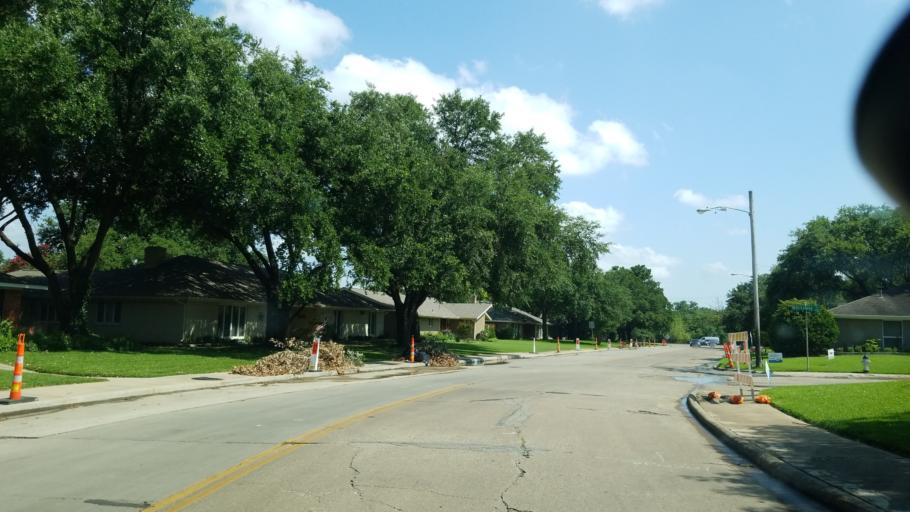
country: US
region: Texas
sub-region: Dallas County
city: Farmers Branch
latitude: 32.8824
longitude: -96.8620
